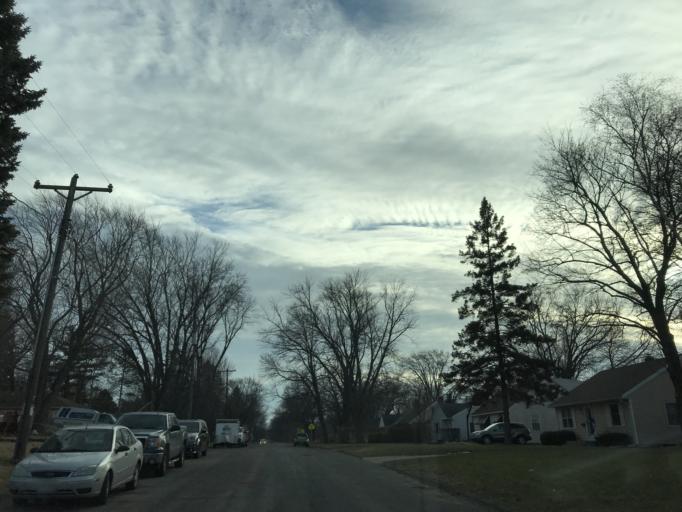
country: US
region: Wisconsin
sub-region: Dane County
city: Monona
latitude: 43.0672
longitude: -89.3360
